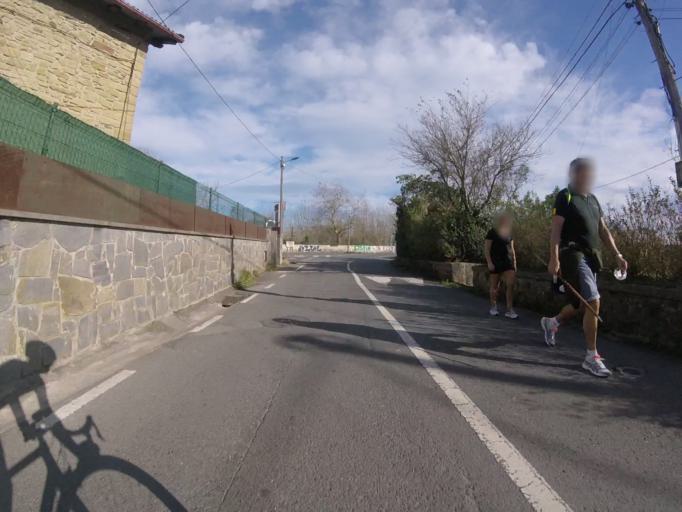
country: ES
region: Basque Country
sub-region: Provincia de Guipuzcoa
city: Usurbil
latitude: 43.3052
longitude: -2.0457
